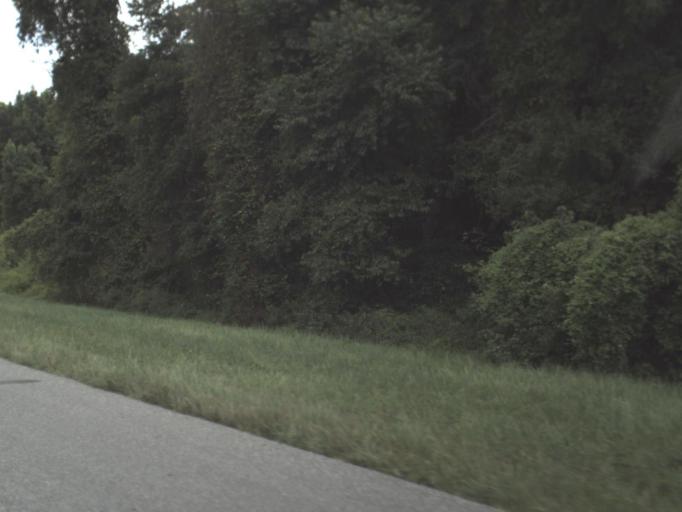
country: US
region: Florida
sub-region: Hernando County
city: Hill 'n Dale
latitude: 28.4464
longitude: -82.2794
